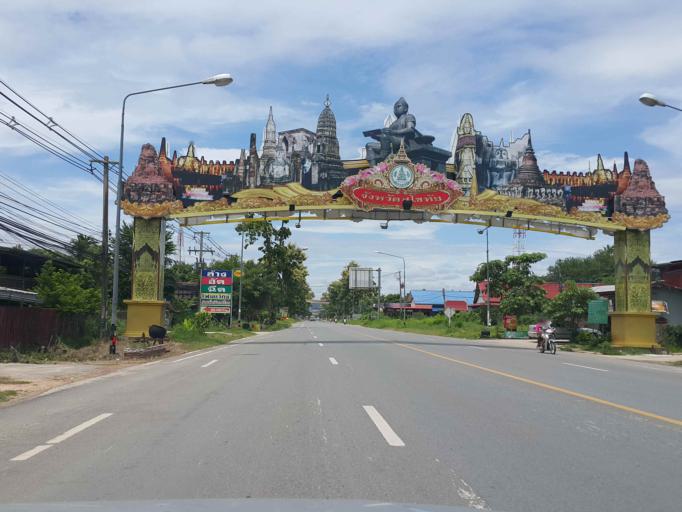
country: TH
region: Sukhothai
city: Ban Na
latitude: 17.0163
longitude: 99.7313
